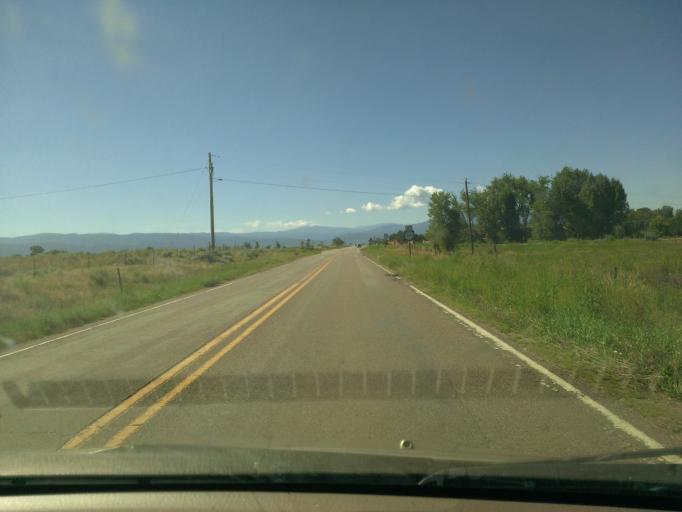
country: US
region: New Mexico
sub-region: Taos County
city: Arroyo Seco
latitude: 36.4979
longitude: -105.5935
